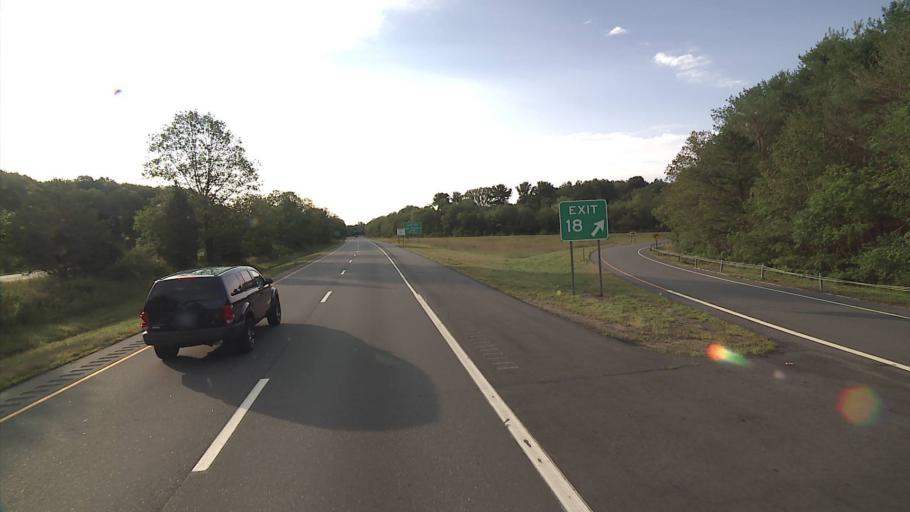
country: US
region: Connecticut
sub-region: New London County
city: Colchester
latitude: 41.5696
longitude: -72.3375
